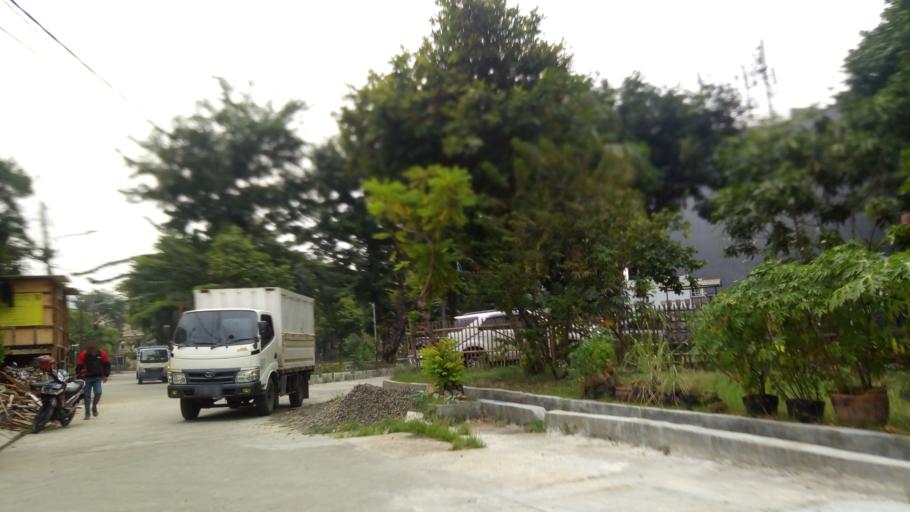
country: ID
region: Jakarta Raya
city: Jakarta
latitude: -6.1498
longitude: 106.8407
